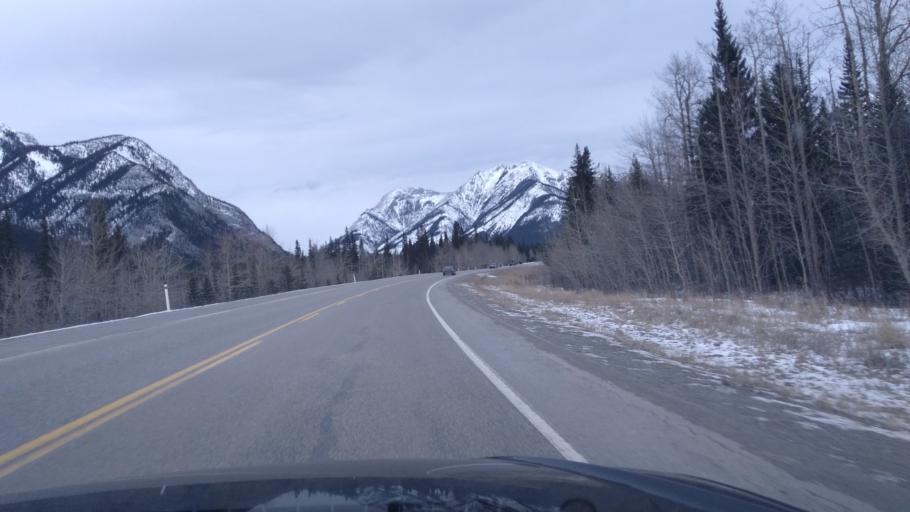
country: CA
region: Alberta
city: Canmore
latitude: 50.9672
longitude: -115.1158
